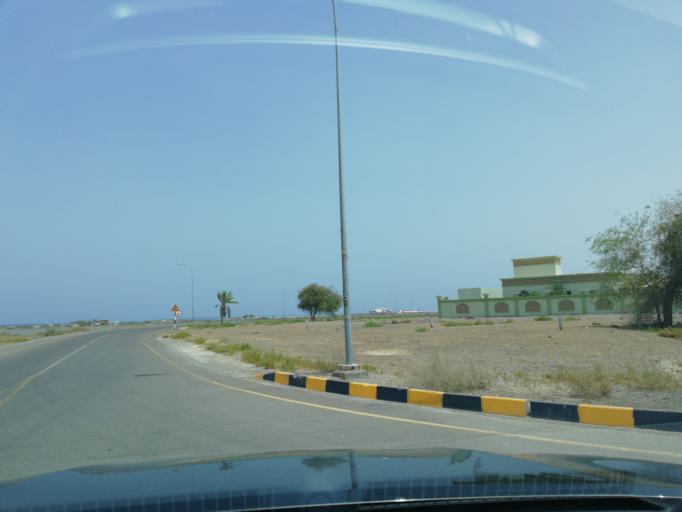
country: OM
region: Al Batinah
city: Shinas
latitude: 24.7538
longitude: 56.4658
